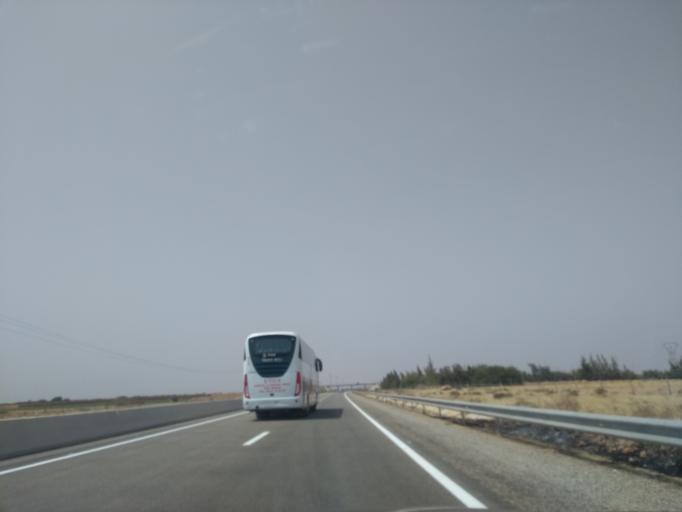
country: MA
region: Marrakech-Tensift-Al Haouz
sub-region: Chichaoua
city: Chichaoua
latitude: 31.3785
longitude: -8.7660
